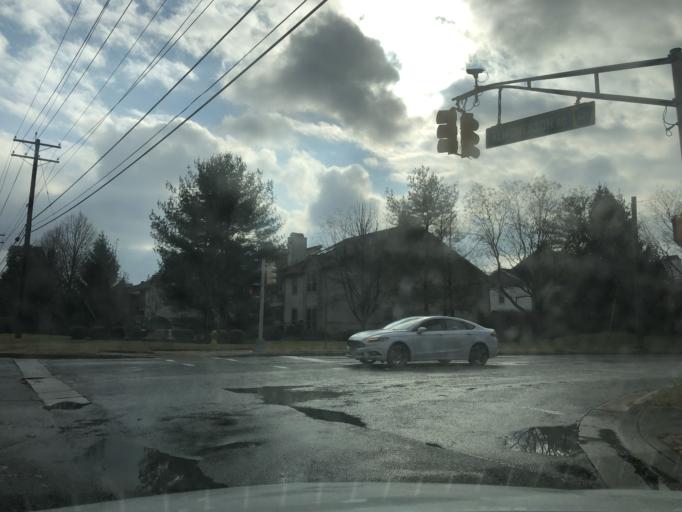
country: US
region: New Jersey
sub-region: Camden County
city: Bellmawr
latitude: 39.8476
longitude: -75.1067
